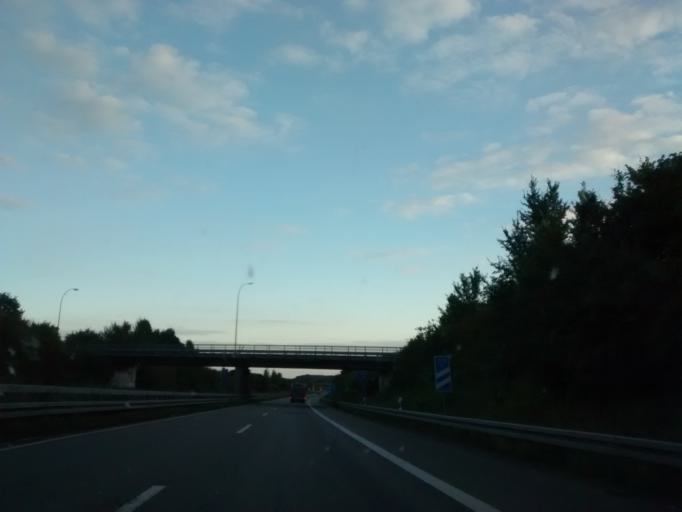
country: DE
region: Lower Saxony
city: Bad Rothenfelde
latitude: 52.1241
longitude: 8.1775
